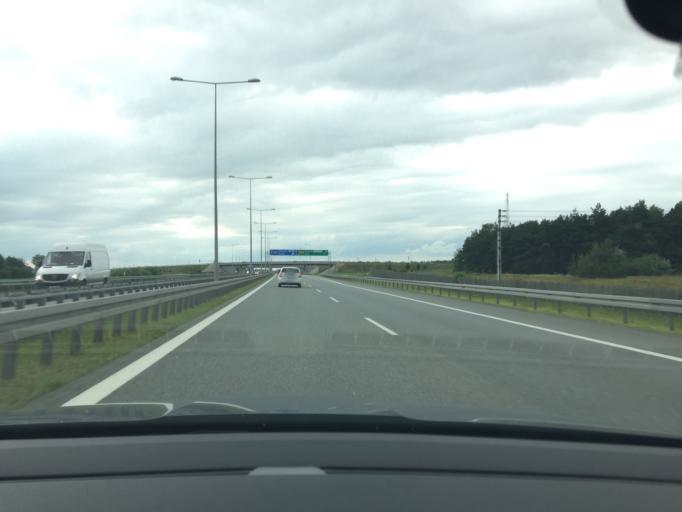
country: PL
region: Greater Poland Voivodeship
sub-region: Powiat poznanski
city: Buk
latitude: 52.3748
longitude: 16.5719
